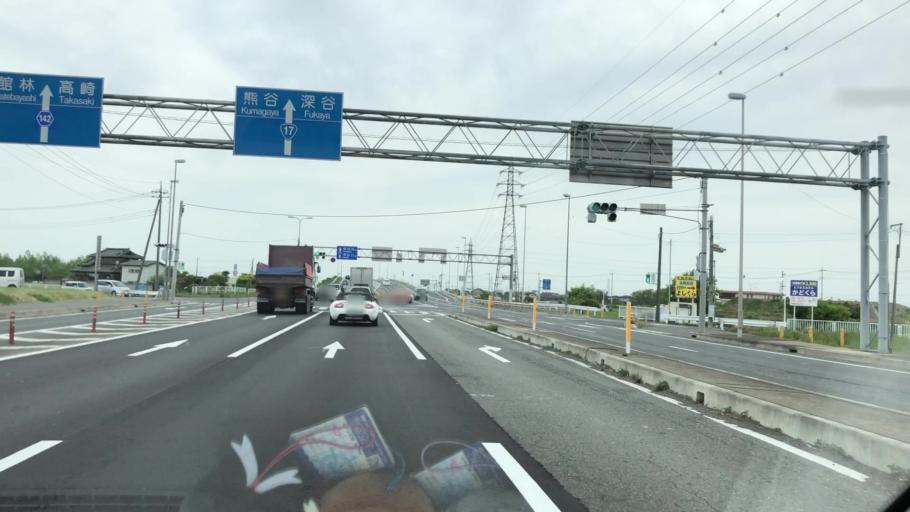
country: JP
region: Gunma
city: Sakai-nakajima
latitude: 36.2640
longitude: 139.2955
